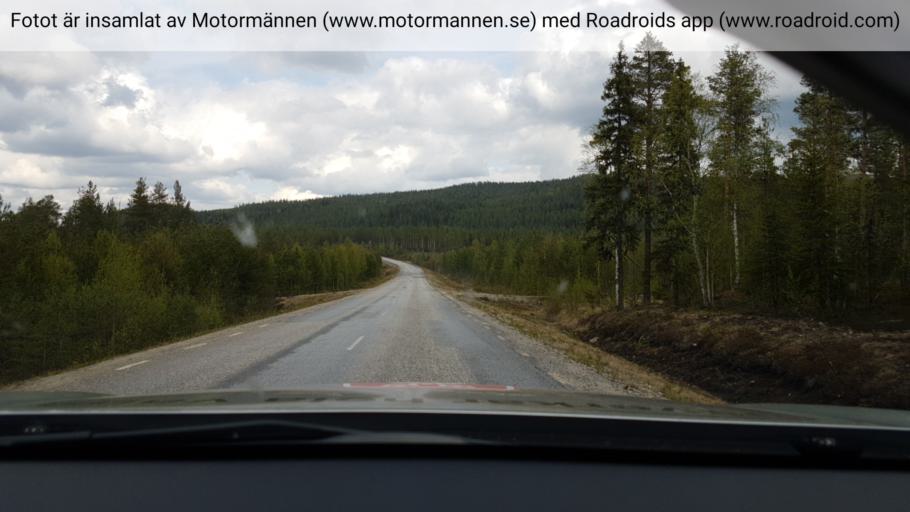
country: SE
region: Vaesternorrland
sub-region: OErnskoeldsviks Kommun
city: Bredbyn
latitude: 63.9262
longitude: 18.4813
